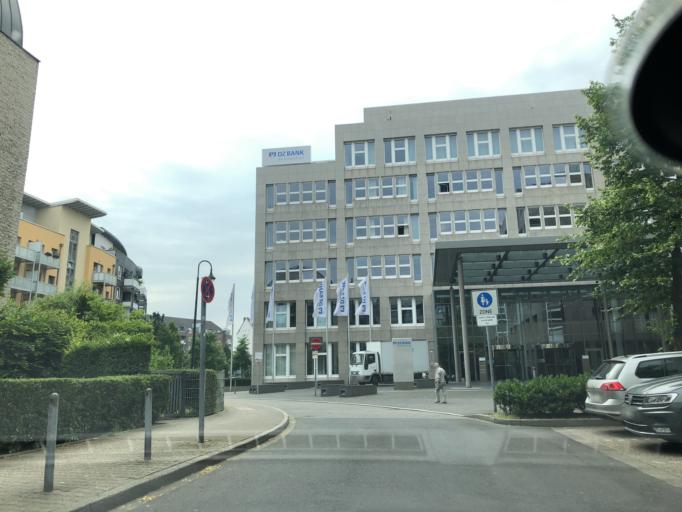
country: DE
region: North Rhine-Westphalia
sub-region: Regierungsbezirk Dusseldorf
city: Dusseldorf
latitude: 51.2196
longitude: 6.7980
